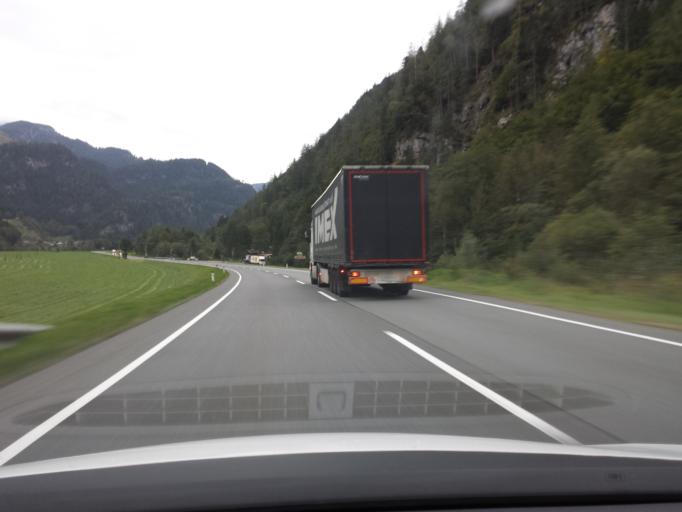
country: AT
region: Salzburg
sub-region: Politischer Bezirk Zell am See
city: Sankt Martin bei Lofer
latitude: 47.5283
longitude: 12.7362
